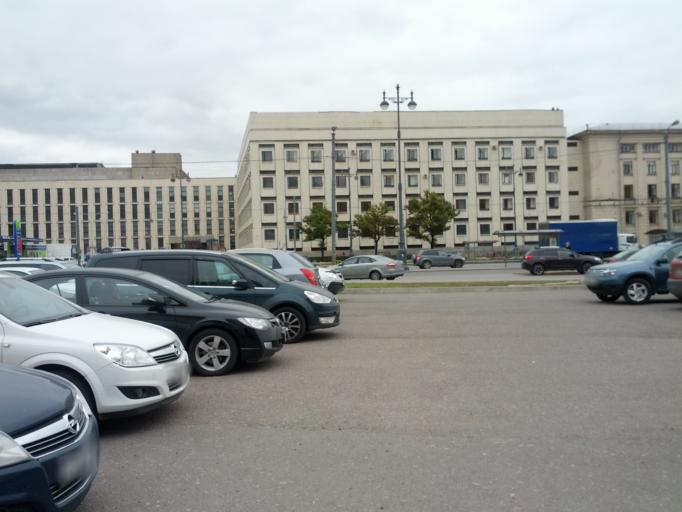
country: RU
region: St.-Petersburg
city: Admiralteisky
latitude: 59.8810
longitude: 30.3186
